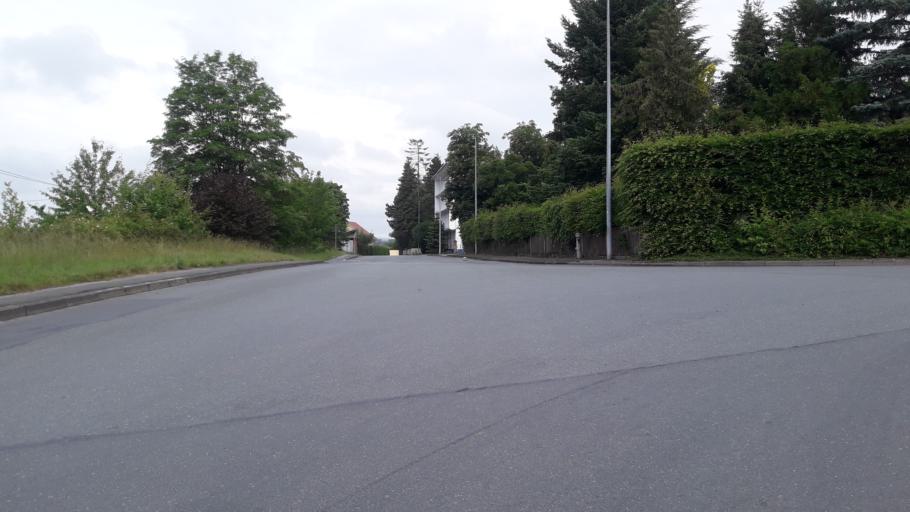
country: DE
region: North Rhine-Westphalia
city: Warburg
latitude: 51.4947
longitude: 9.1575
